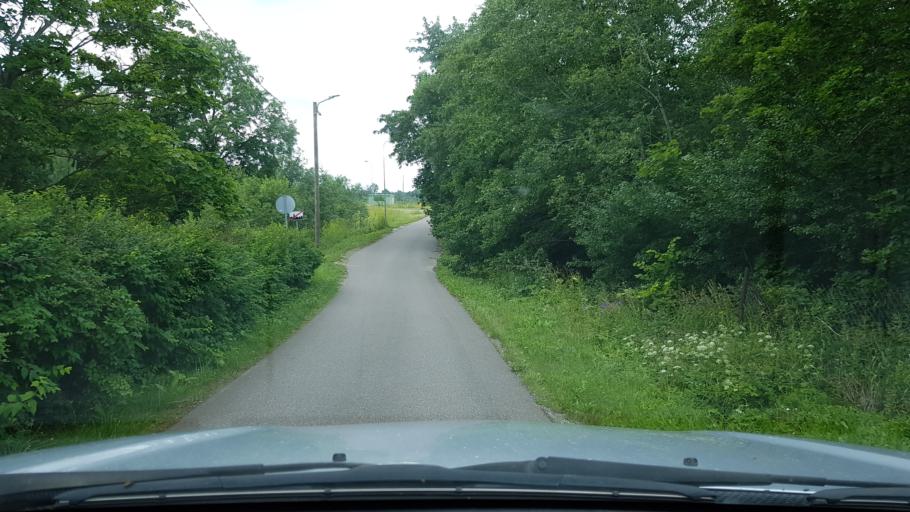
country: EE
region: Ida-Virumaa
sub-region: Narva linn
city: Narva
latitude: 59.3967
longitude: 28.1234
